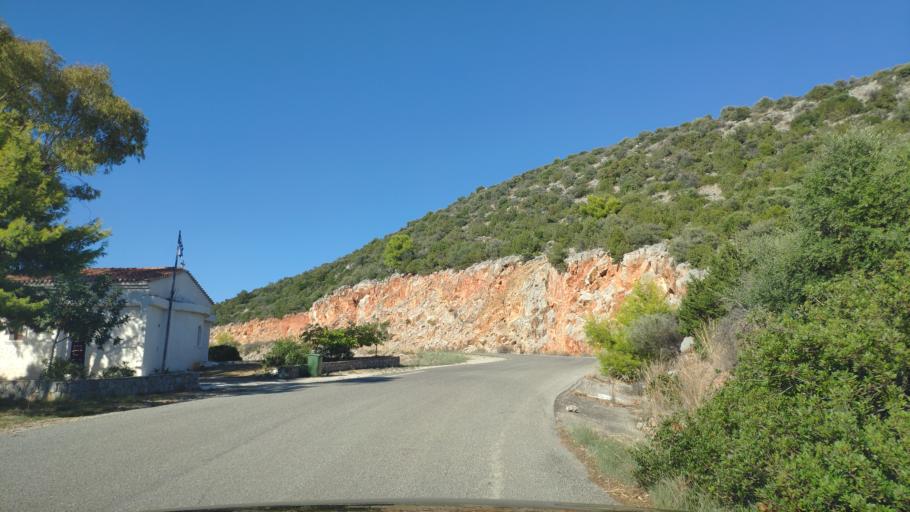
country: GR
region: Attica
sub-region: Nomos Piraios
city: Galatas
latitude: 37.5616
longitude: 23.3641
